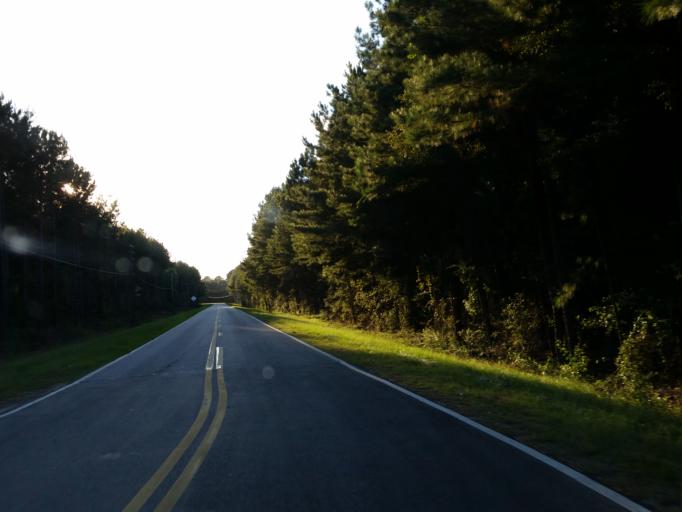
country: US
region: Georgia
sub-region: Crisp County
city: Cordele
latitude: 32.0059
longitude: -83.7396
